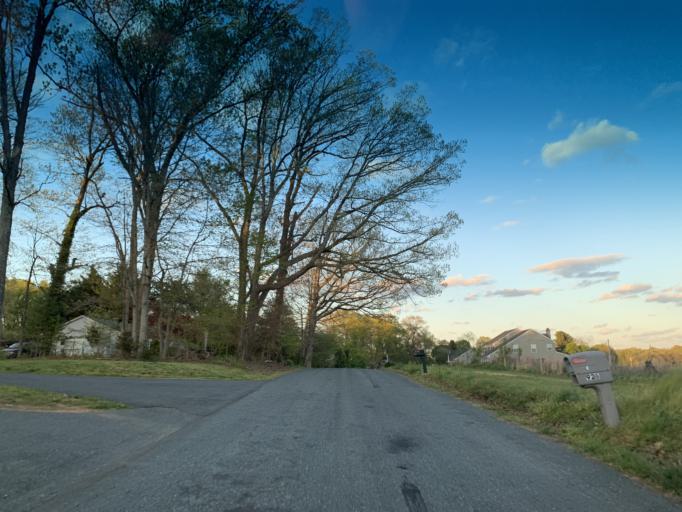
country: US
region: Maryland
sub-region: Harford County
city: Jarrettsville
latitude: 39.6578
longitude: -76.4205
